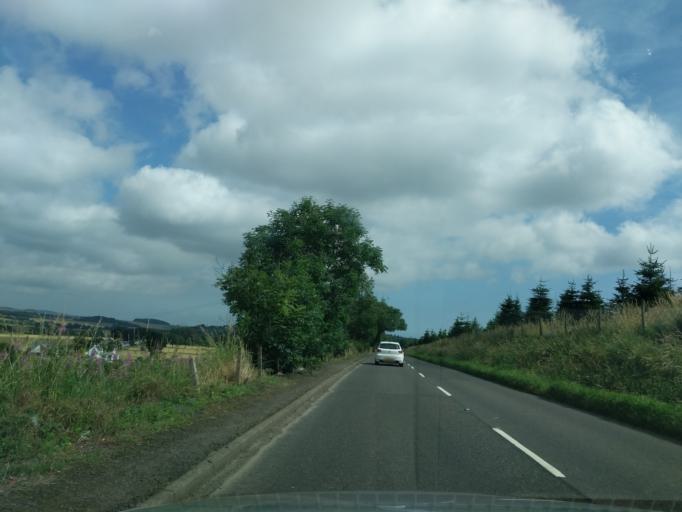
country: GB
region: Scotland
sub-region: Angus
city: Muirhead
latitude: 56.4991
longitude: -3.0844
